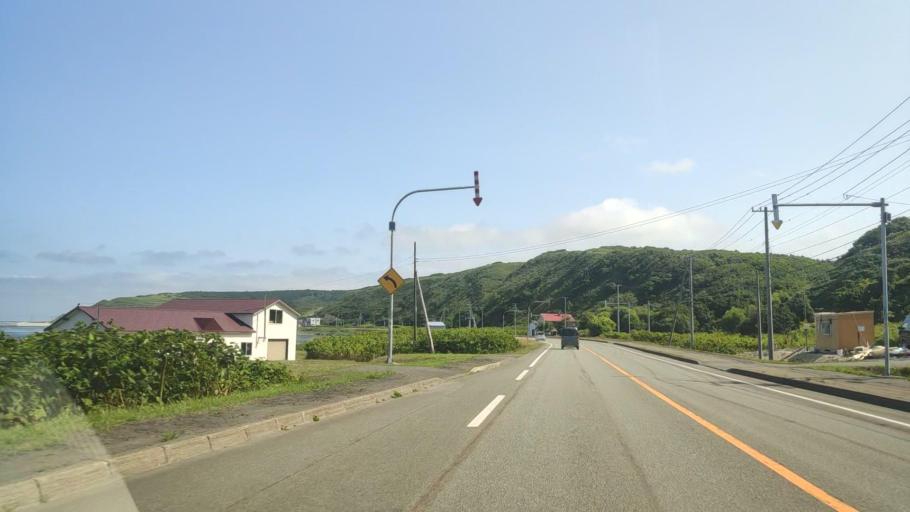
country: JP
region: Hokkaido
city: Makubetsu
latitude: 45.4790
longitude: 141.8777
